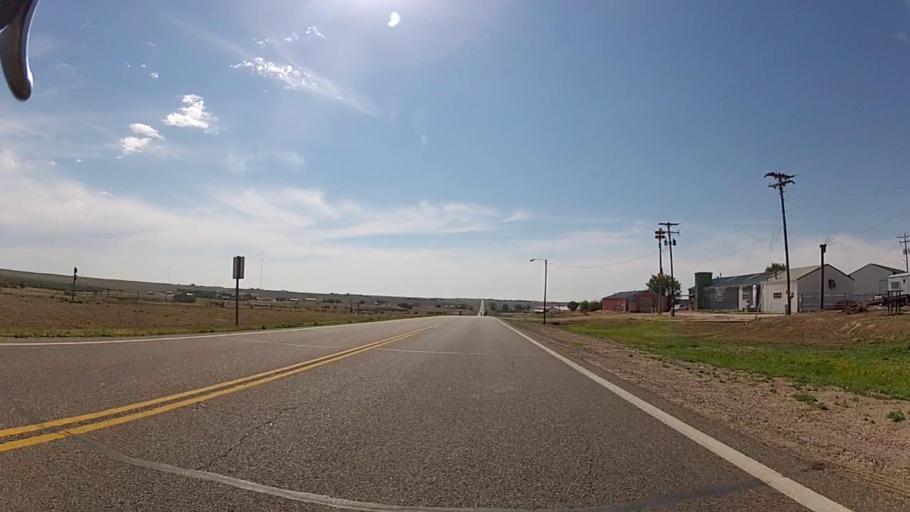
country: US
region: Kansas
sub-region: Grant County
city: Ulysses
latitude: 37.5735
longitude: -101.3385
